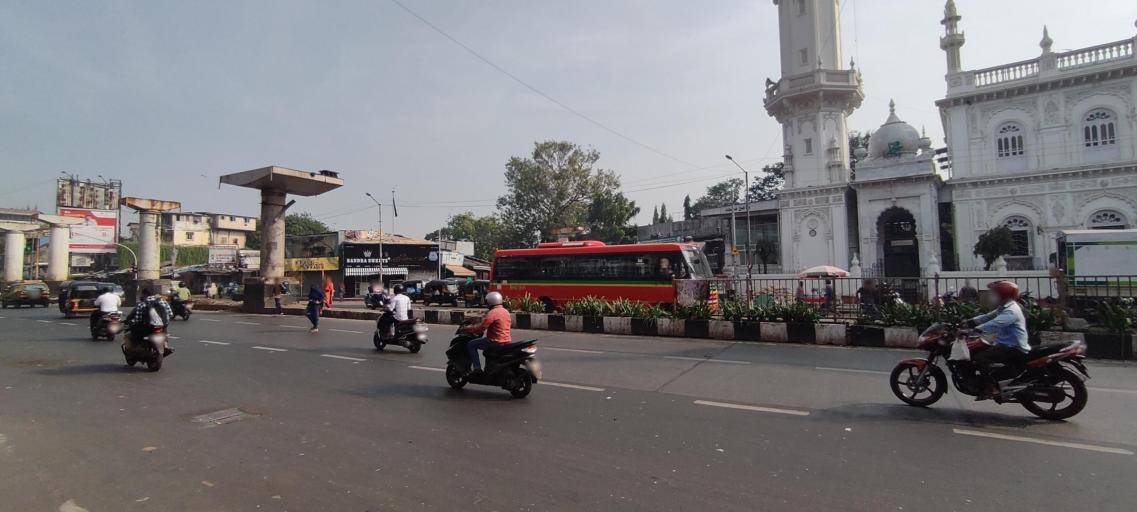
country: IN
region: Maharashtra
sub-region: Mumbai Suburban
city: Mumbai
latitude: 19.0519
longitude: 72.8381
